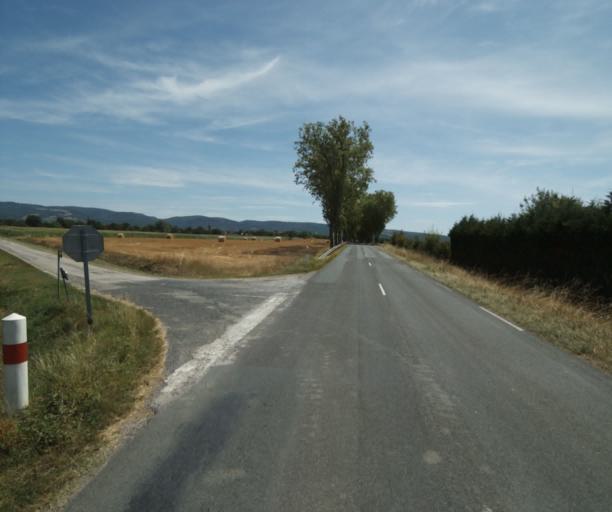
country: FR
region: Midi-Pyrenees
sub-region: Departement de la Haute-Garonne
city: Revel
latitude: 43.4967
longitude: 2.0125
